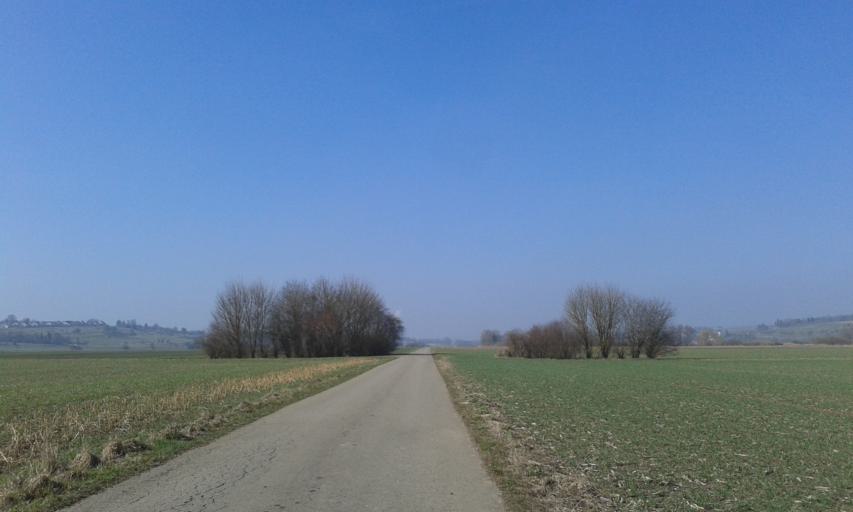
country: DE
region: Baden-Wuerttemberg
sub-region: Tuebingen Region
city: Opfingen
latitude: 48.2758
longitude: 9.7948
